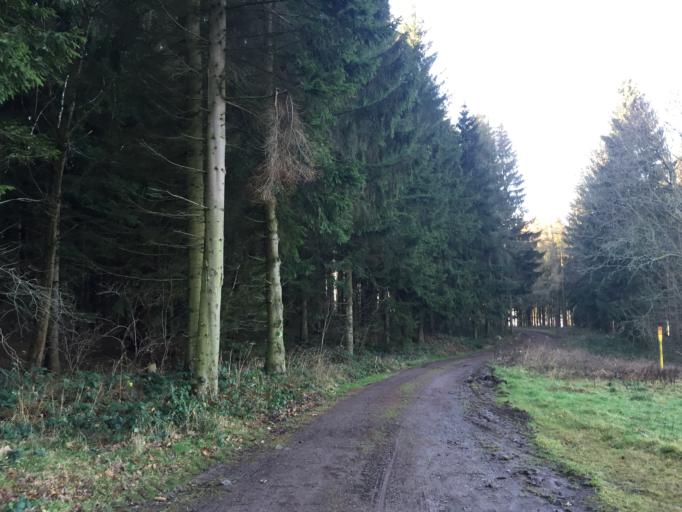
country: DE
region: Thuringia
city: Schmorda
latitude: 50.6583
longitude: 11.5900
